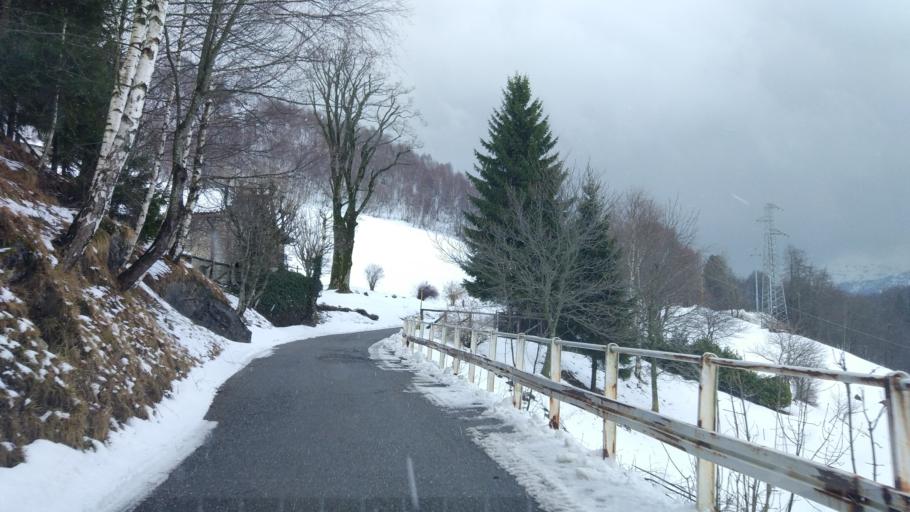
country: IT
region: Lombardy
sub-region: Provincia di Lecco
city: Moggio
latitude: 45.9054
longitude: 9.4955
